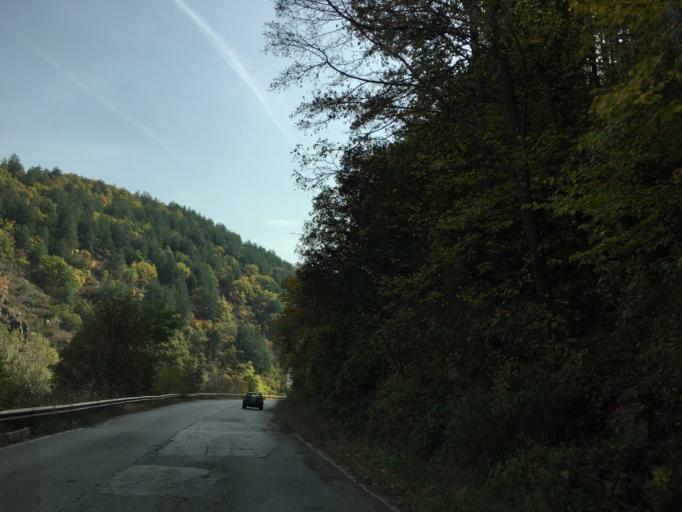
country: BG
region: Sofia-Capital
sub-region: Stolichna Obshtina
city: Sofia
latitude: 42.5779
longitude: 23.4263
